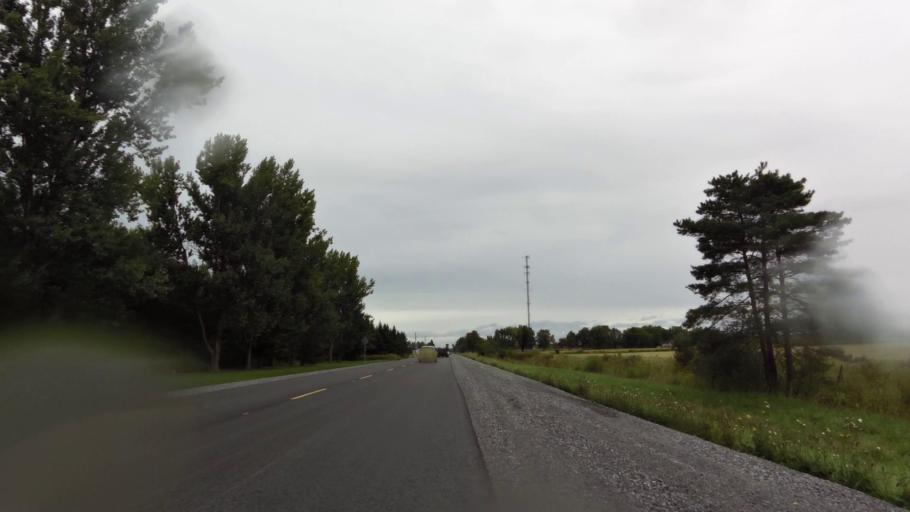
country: CA
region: Ontario
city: Bells Corners
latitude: 45.1358
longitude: -75.6328
